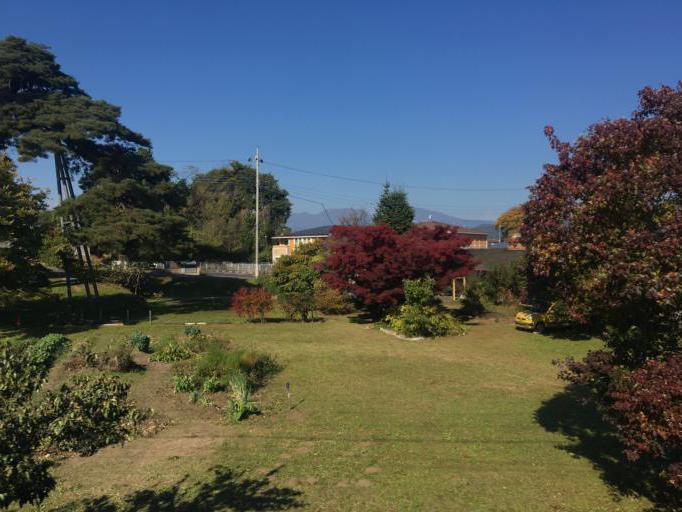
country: JP
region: Gunma
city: Kiryu
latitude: 36.4056
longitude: 139.3120
